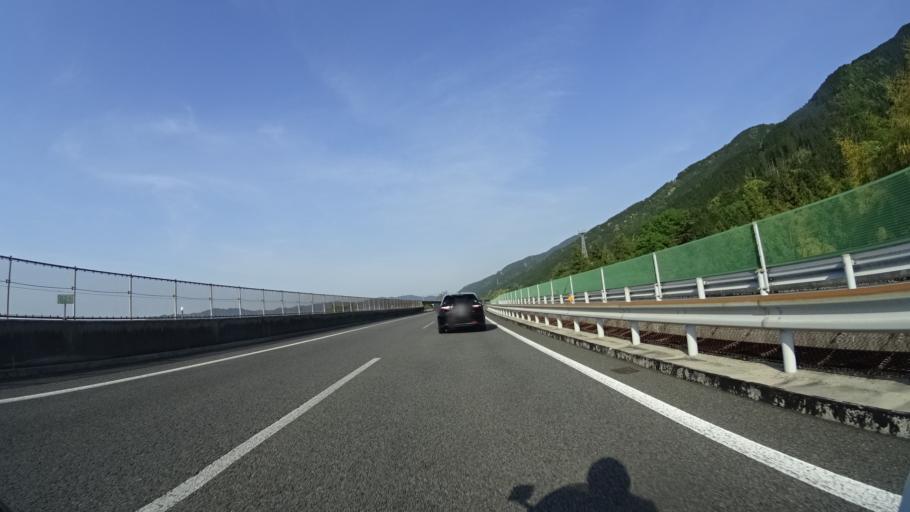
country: JP
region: Ehime
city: Niihama
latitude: 33.9170
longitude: 133.2892
